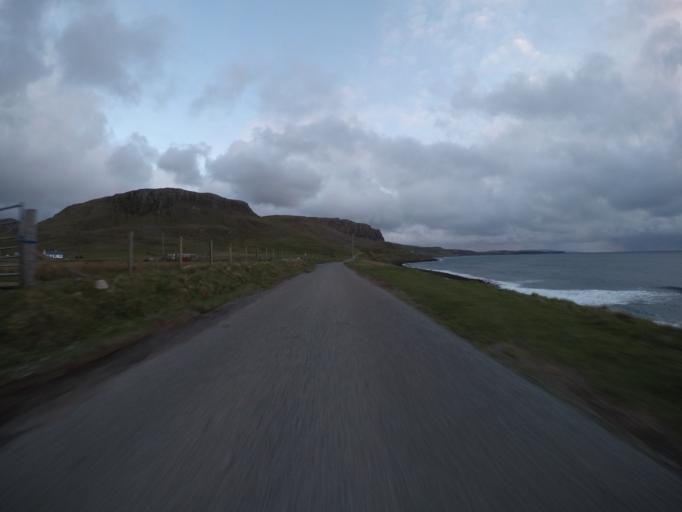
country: GB
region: Scotland
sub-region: Highland
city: Portree
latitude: 57.6798
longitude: -6.3446
